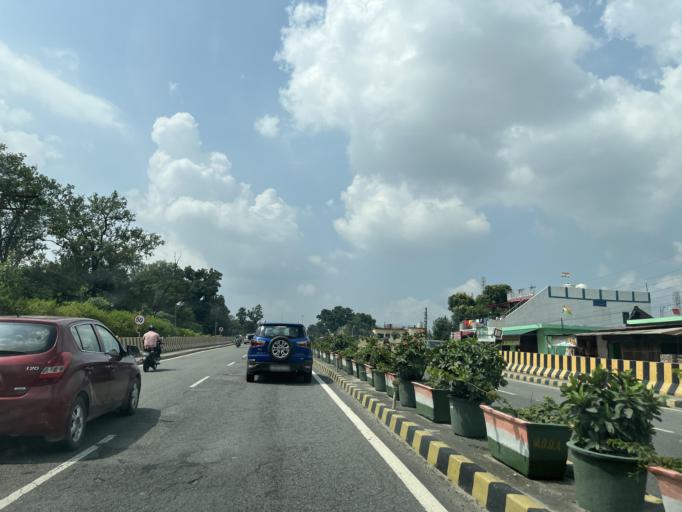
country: IN
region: Uttarakhand
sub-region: Dehradun
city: Raipur
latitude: 30.2737
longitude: 78.0771
